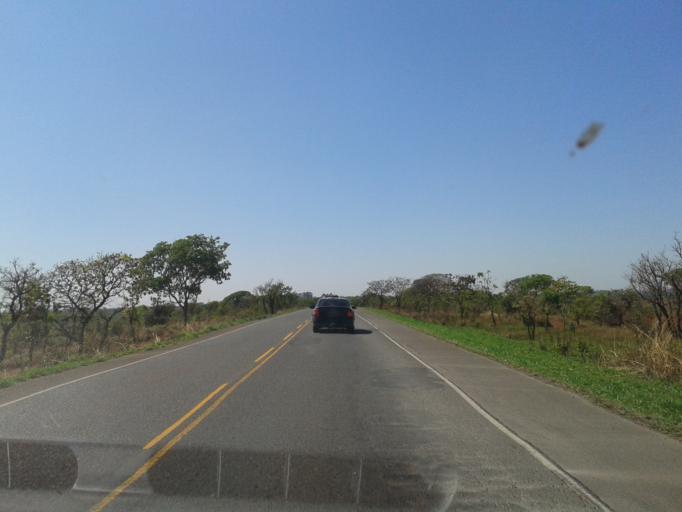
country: BR
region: Minas Gerais
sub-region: Uberlandia
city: Uberlandia
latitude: -19.0440
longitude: -48.0534
